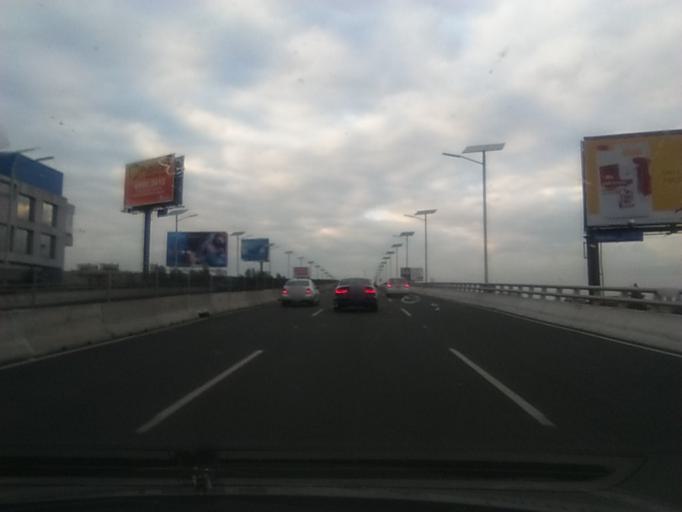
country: MX
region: Mexico City
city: Polanco
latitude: 19.3944
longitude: -99.1885
